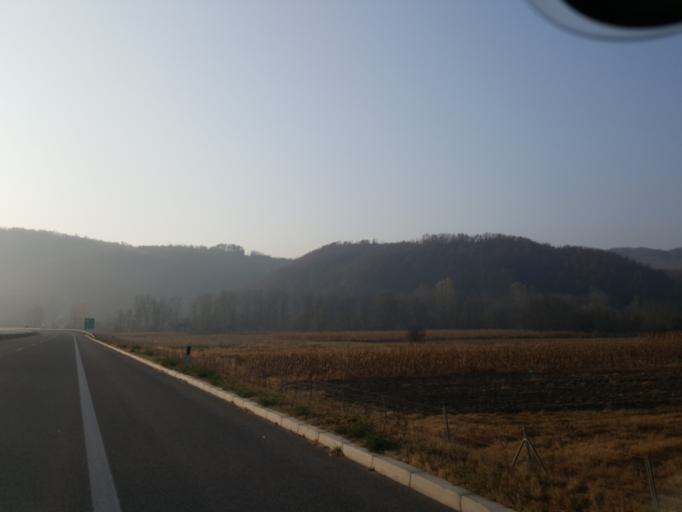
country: RS
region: Central Serbia
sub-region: Jablanicki Okrug
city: Vlasotince
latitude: 42.9009
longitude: 22.0510
